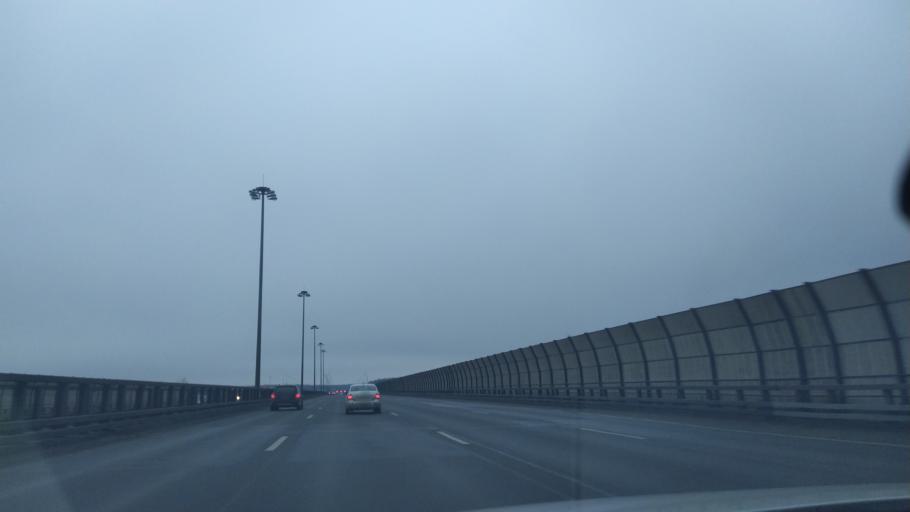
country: RU
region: St.-Petersburg
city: Krasnogvargeisky
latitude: 59.9785
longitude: 30.5273
